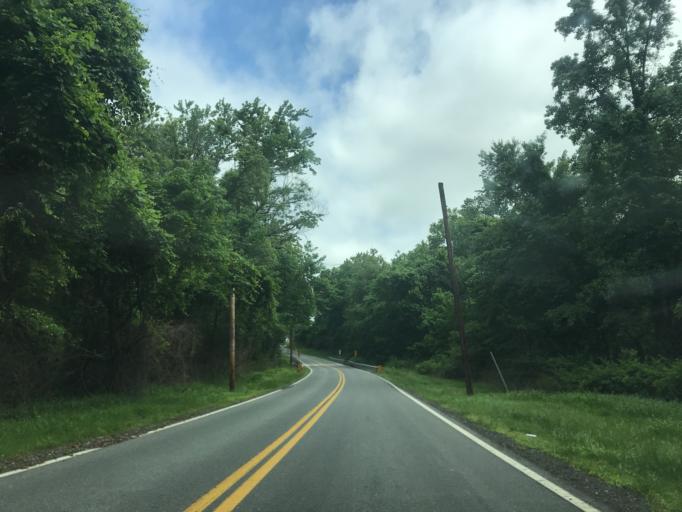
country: US
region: Maryland
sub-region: Caroline County
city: Ridgely
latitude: 38.8901
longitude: -75.9605
